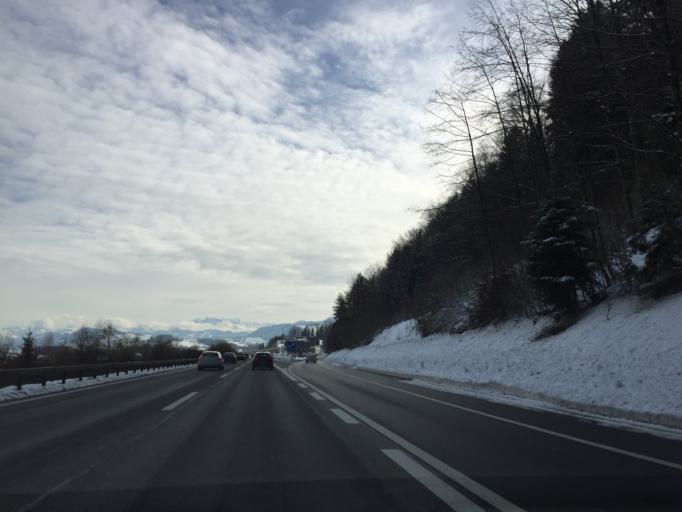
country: CH
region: Zurich
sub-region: Bezirk Horgen
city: Horgen / Allmend
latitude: 47.2419
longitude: 8.6068
